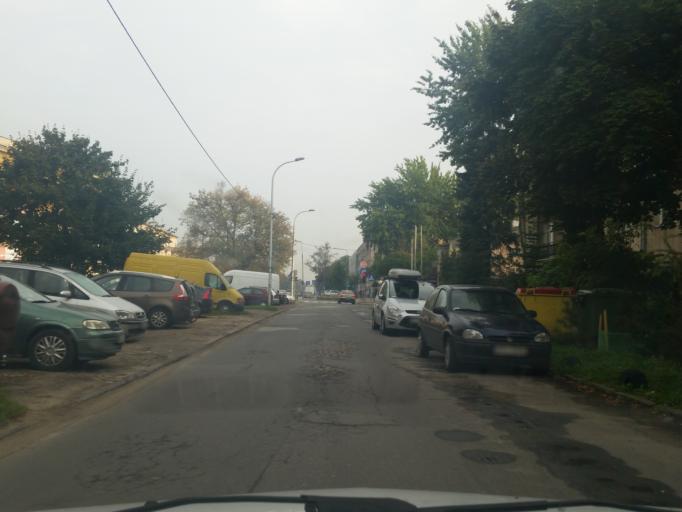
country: PL
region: Masovian Voivodeship
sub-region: Warszawa
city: Mokotow
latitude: 52.1855
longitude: 21.0250
